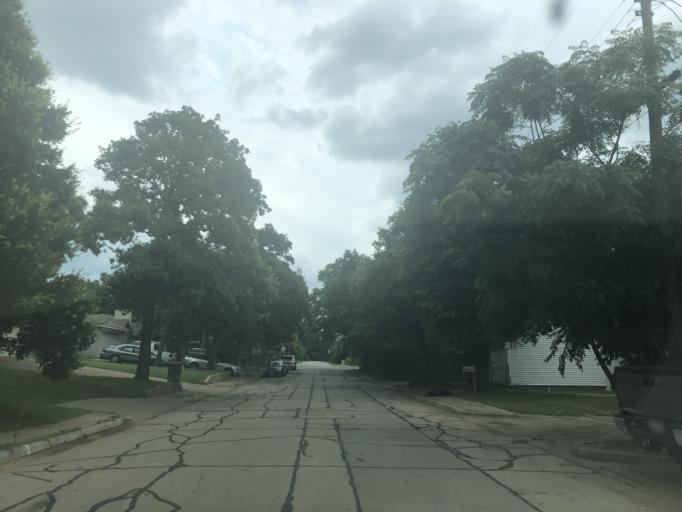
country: US
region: Texas
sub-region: Dallas County
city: Irving
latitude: 32.8036
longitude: -96.9309
